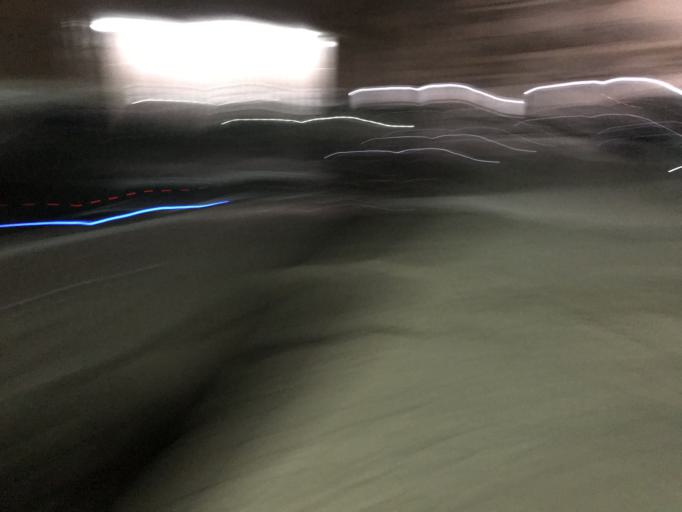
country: IT
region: Apulia
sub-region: Provincia di Bari
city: Corato
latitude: 41.1575
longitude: 16.4026
